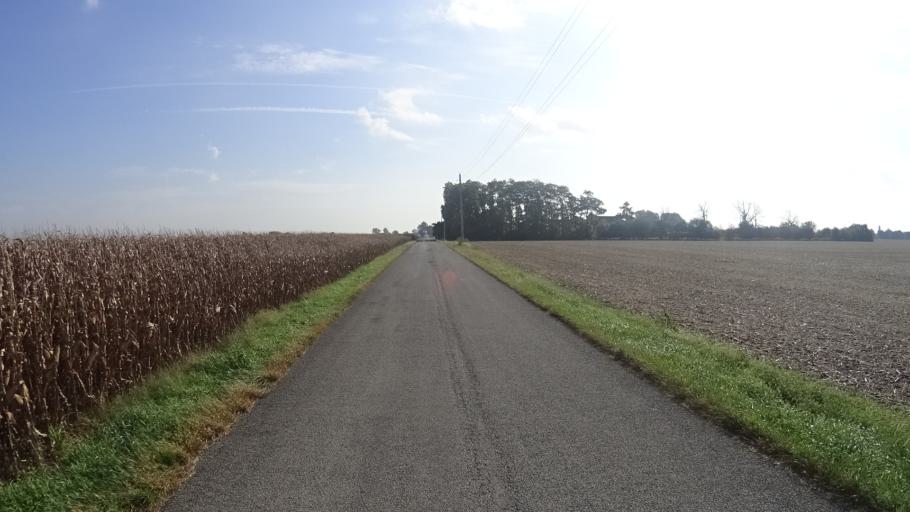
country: US
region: Indiana
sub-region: Madison County
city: Lapel
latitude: 40.0457
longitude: -85.8304
